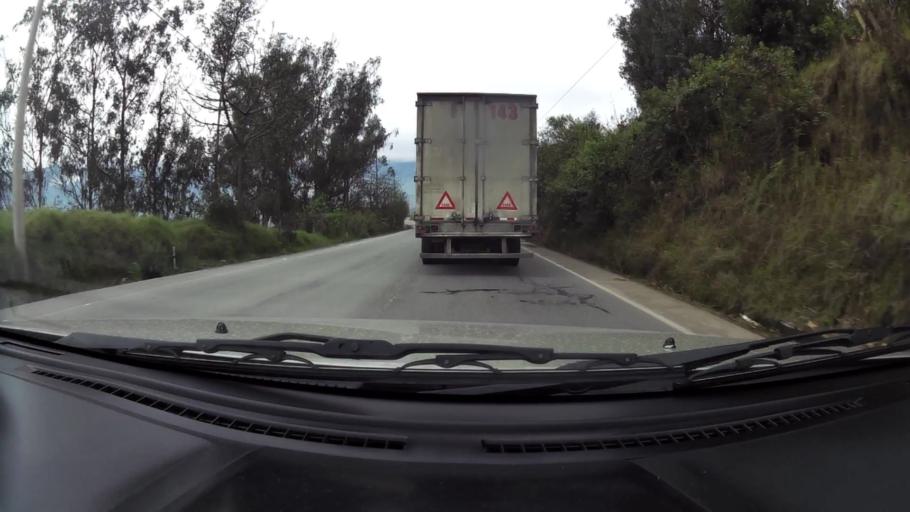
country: EC
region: Chimborazo
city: Alausi
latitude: -2.3070
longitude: -78.9287
